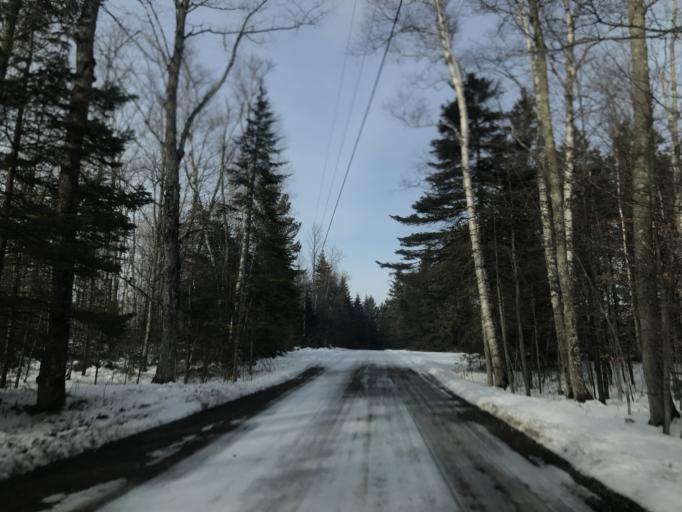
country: US
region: Wisconsin
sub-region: Door County
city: Sturgeon Bay
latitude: 45.1480
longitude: -87.0539
